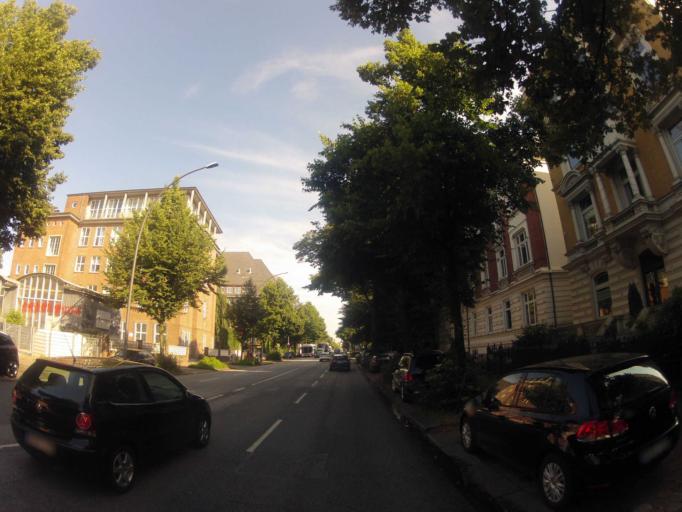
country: DE
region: Hamburg
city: Borgfelde
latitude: 53.5679
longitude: 10.0300
